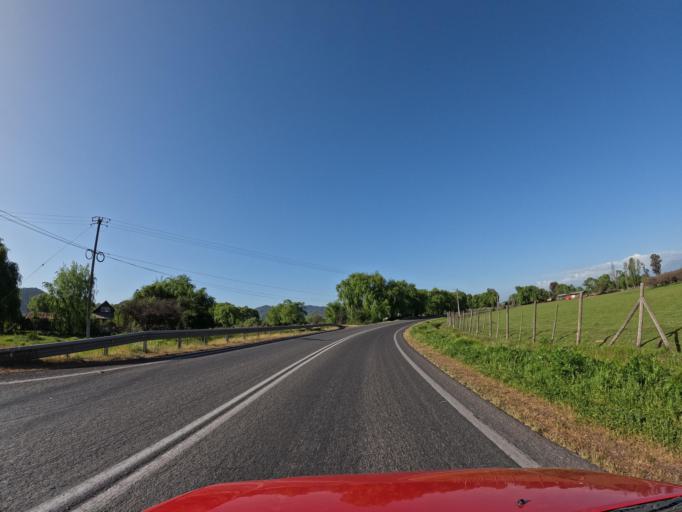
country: CL
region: Maule
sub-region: Provincia de Curico
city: Teno
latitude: -34.8498
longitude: -71.1927
